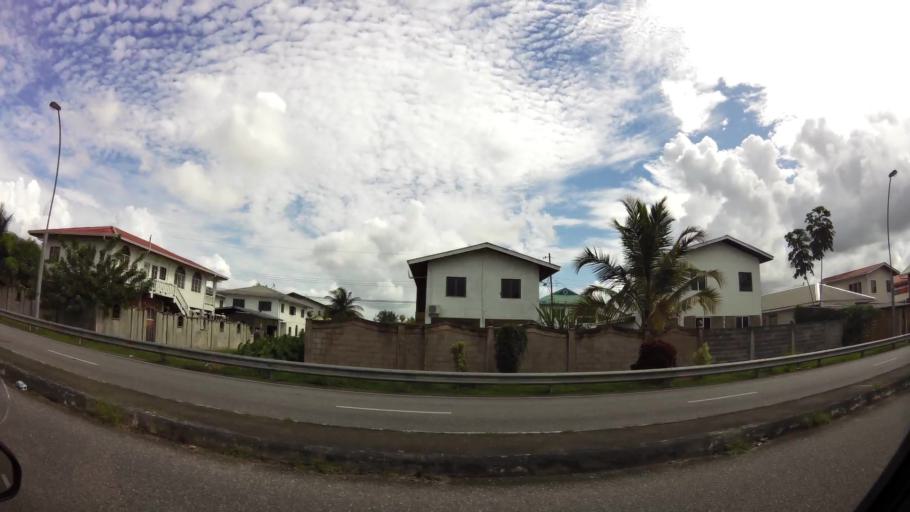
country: TT
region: Chaguanas
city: Chaguanas
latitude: 10.5088
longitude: -61.3945
